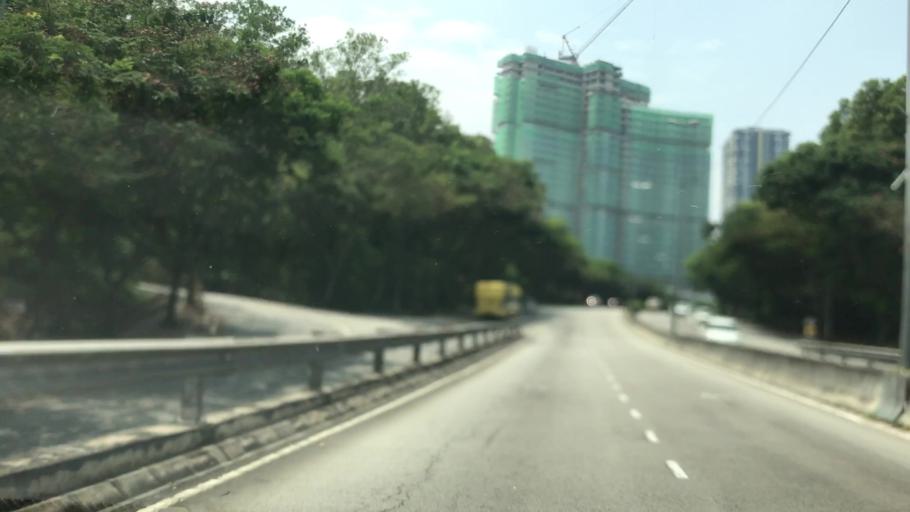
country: MY
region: Selangor
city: Subang Jaya
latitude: 3.0244
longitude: 101.6196
